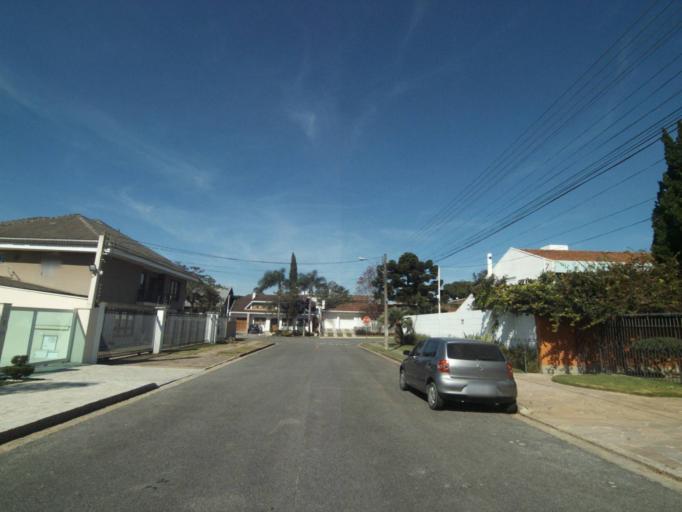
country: BR
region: Parana
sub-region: Curitiba
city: Curitiba
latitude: -25.4148
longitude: -49.2384
